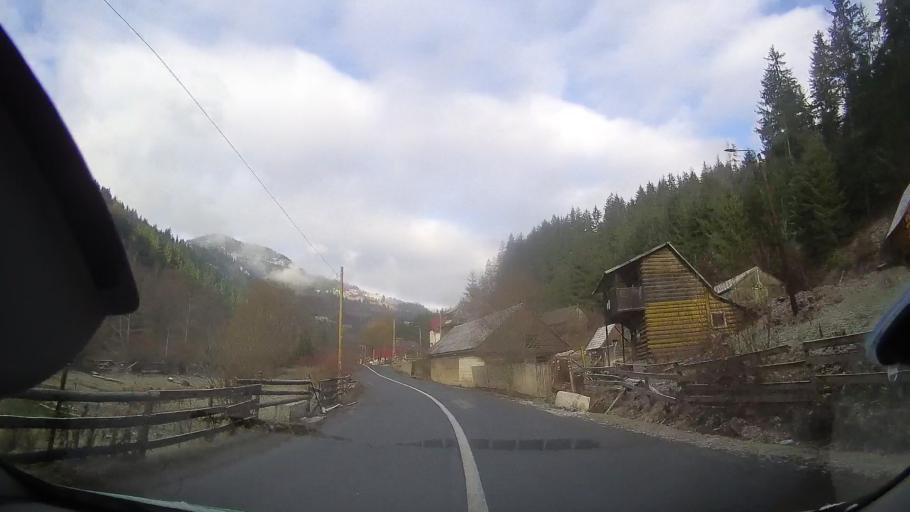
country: RO
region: Alba
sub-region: Comuna Albac
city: Albac
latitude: 46.4597
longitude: 22.9752
